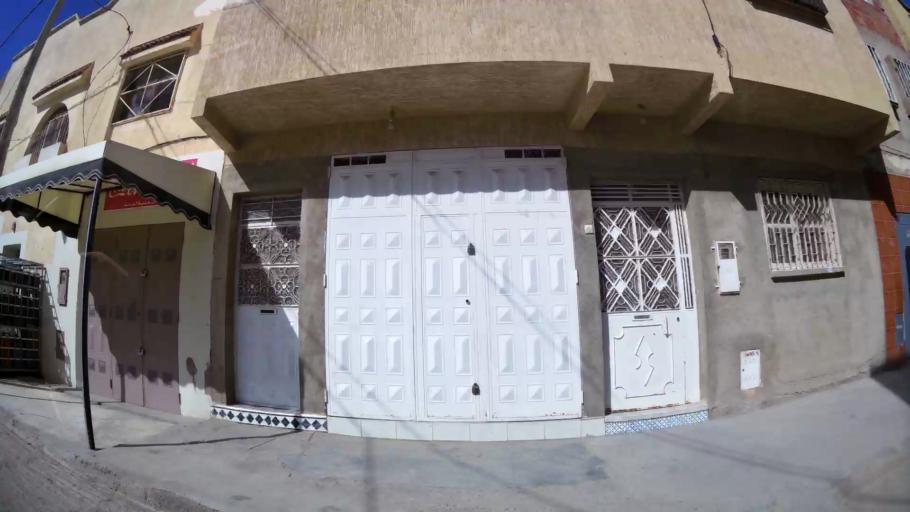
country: MA
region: Oriental
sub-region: Oujda-Angad
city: Oujda
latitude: 34.7136
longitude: -1.8830
